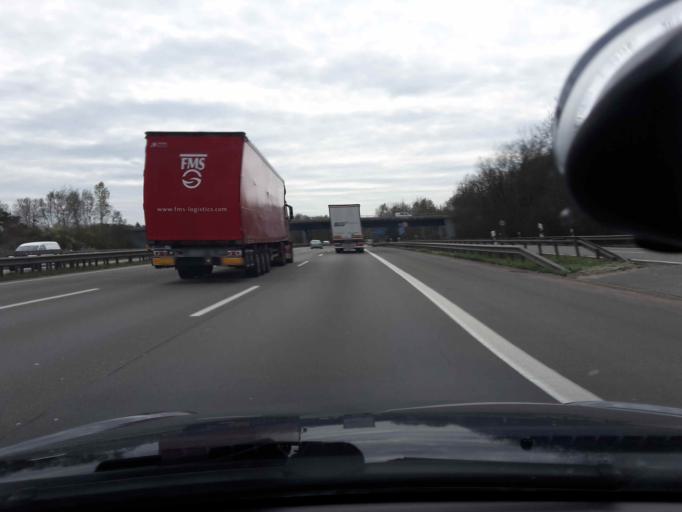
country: DE
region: Lower Saxony
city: Harmstorf
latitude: 53.3880
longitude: 10.0213
